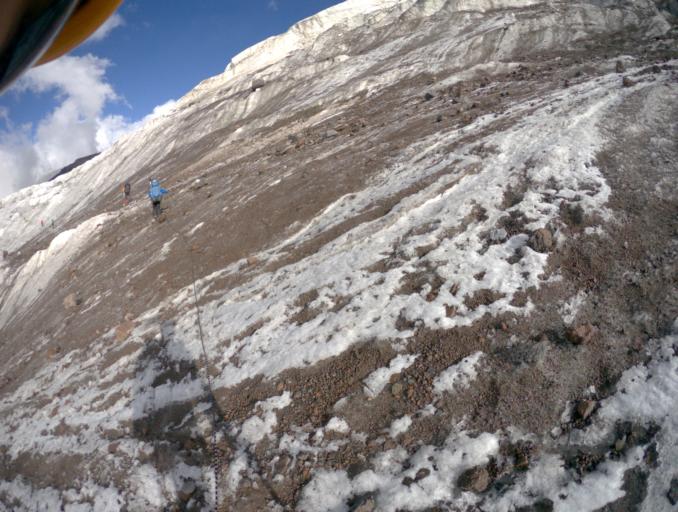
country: RU
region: Kabardino-Balkariya
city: Terskol
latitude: 43.3844
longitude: 42.4205
